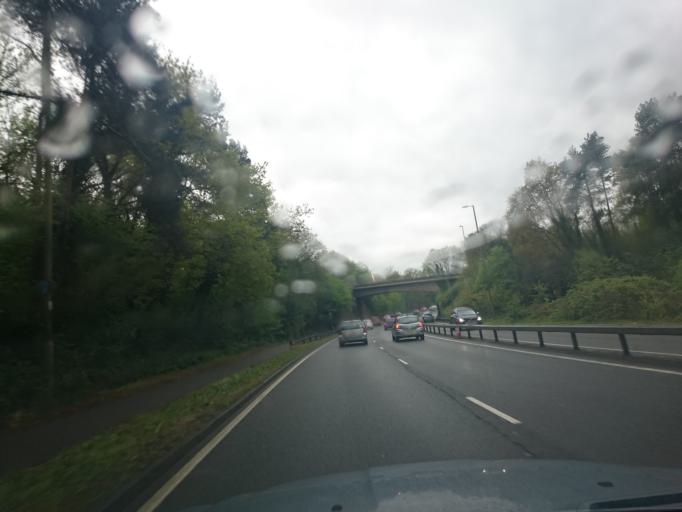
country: GB
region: England
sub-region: Surrey
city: Farnham
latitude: 51.2107
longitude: -0.7957
